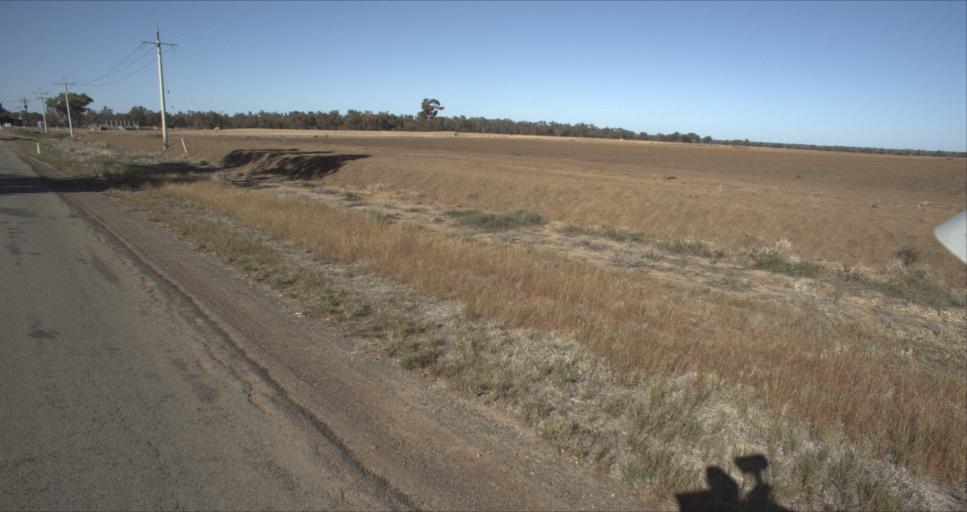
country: AU
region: New South Wales
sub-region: Leeton
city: Leeton
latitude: -34.6032
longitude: 146.2573
